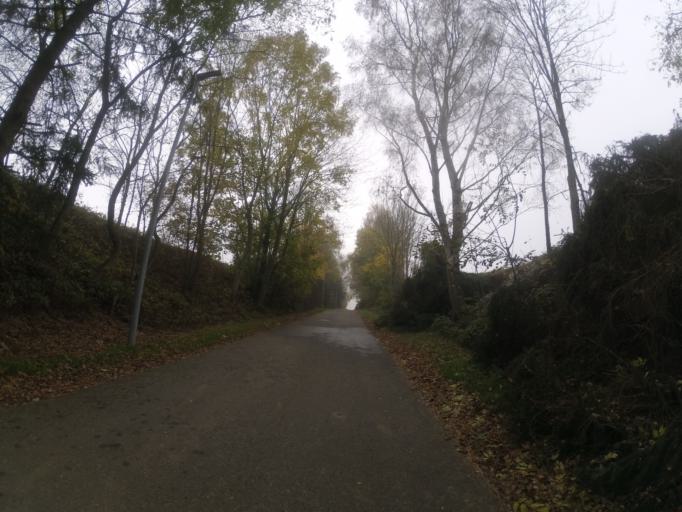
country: DE
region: Baden-Wuerttemberg
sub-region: Tuebingen Region
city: Staig
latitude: 48.3347
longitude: 10.0059
